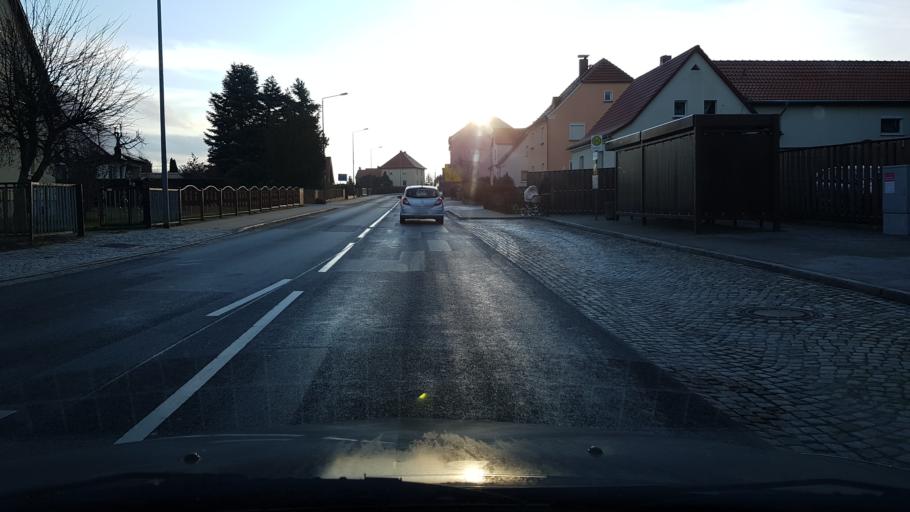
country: DE
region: Saxony
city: Radibor
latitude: 51.2130
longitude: 14.3931
